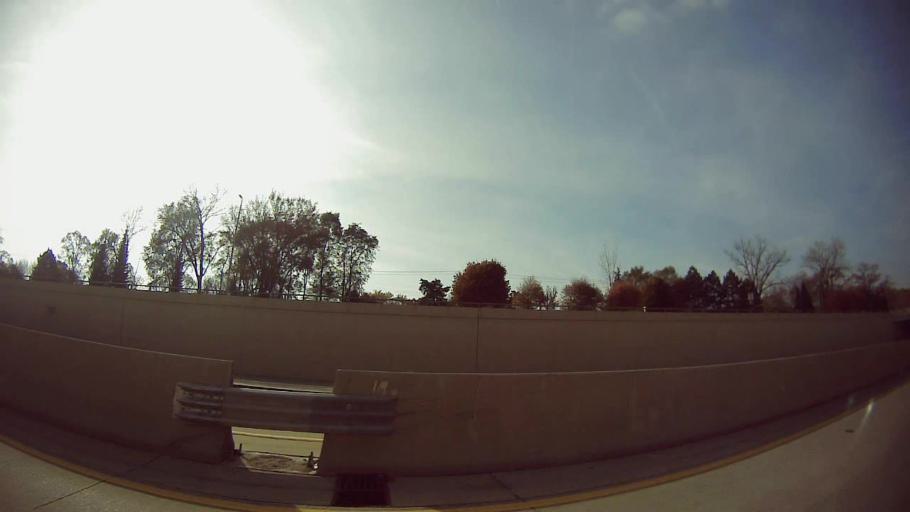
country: US
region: Michigan
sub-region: Oakland County
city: Southfield
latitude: 42.4510
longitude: -83.2101
